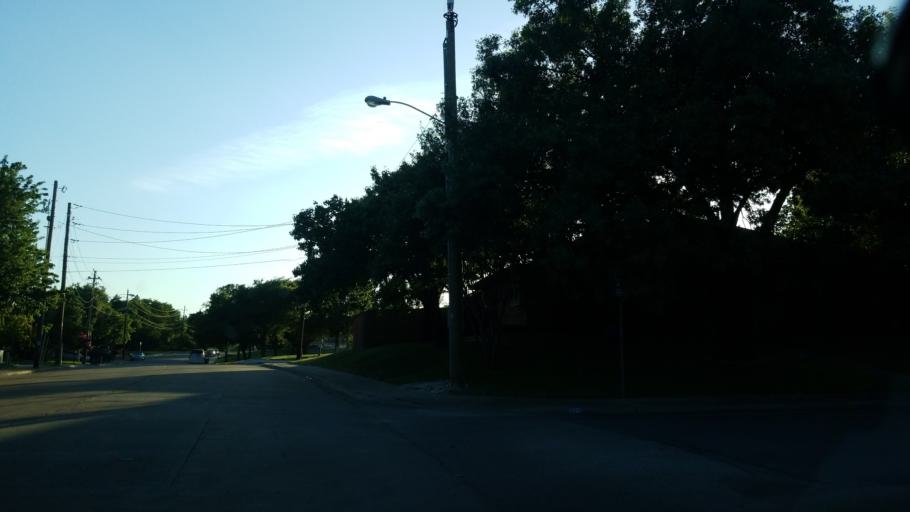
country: US
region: Texas
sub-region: Dallas County
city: Balch Springs
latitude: 32.7858
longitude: -96.6973
